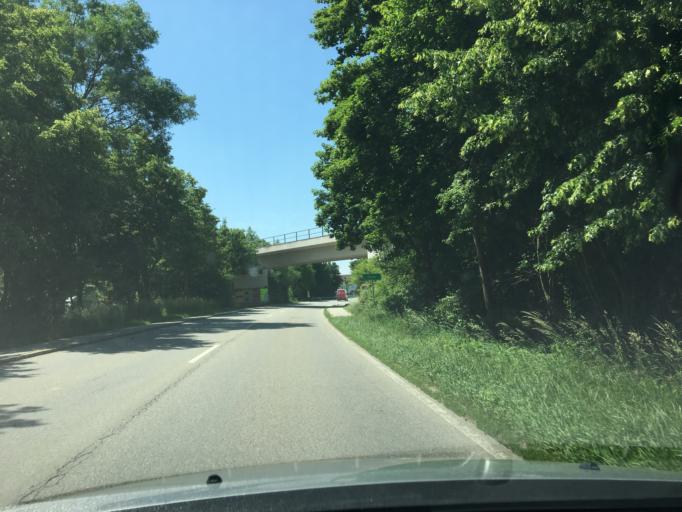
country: DE
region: Bavaria
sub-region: Upper Bavaria
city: Neumarkt-Sankt Veit
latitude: 48.3538
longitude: 12.4944
